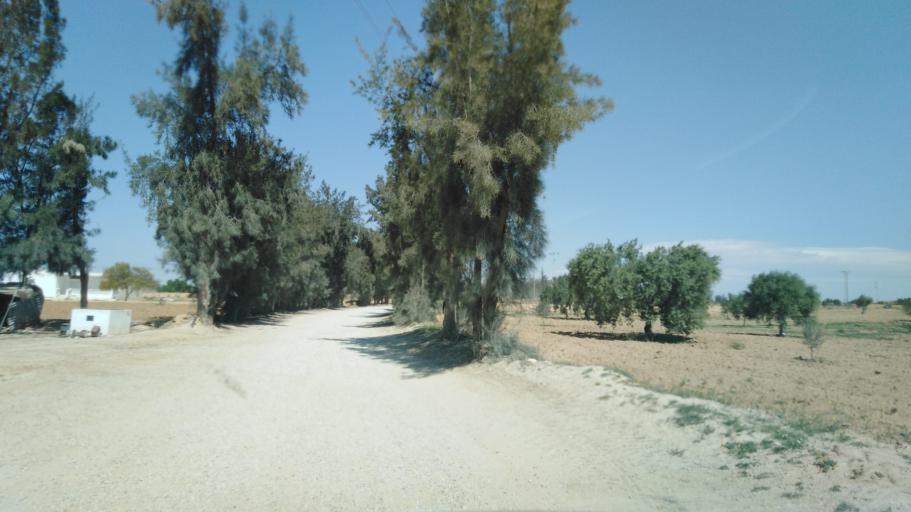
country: TN
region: Safaqis
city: Sfax
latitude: 34.7564
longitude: 10.5298
